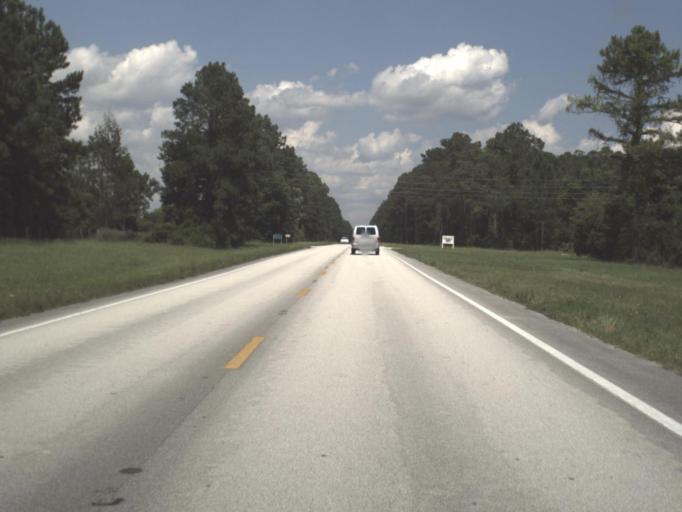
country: US
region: Florida
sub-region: Bradford County
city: Starke
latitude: 29.9385
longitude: -82.0380
